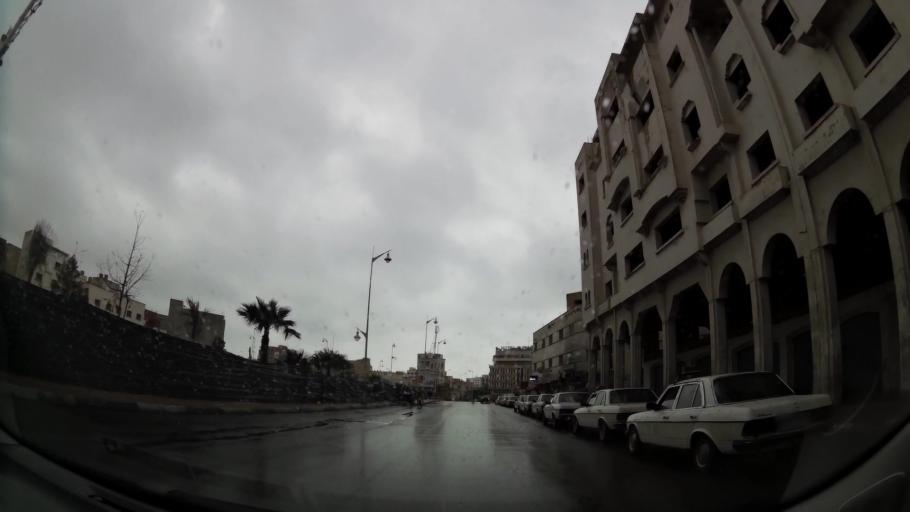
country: MA
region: Oriental
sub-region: Nador
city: Nador
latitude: 35.1784
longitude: -2.9291
